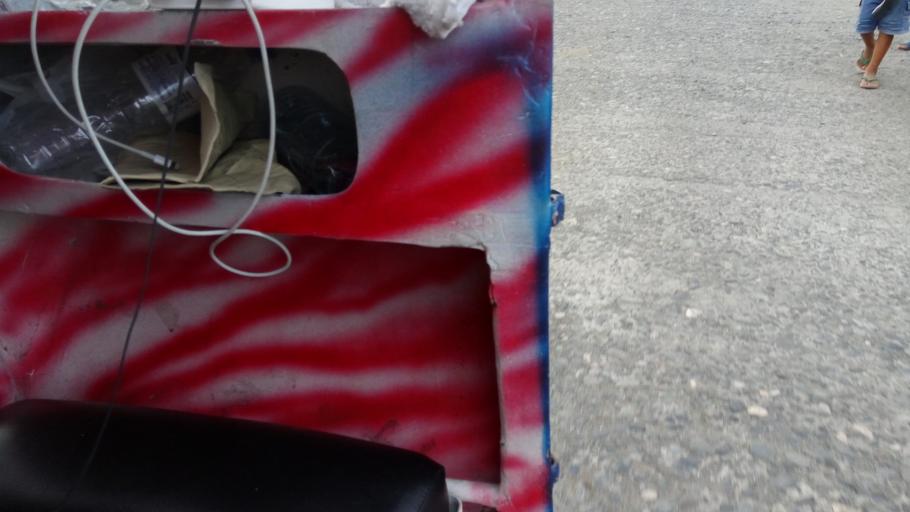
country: PH
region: Ilocos
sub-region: Province of La Union
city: Namboongan
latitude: 16.2935
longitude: 120.3813
